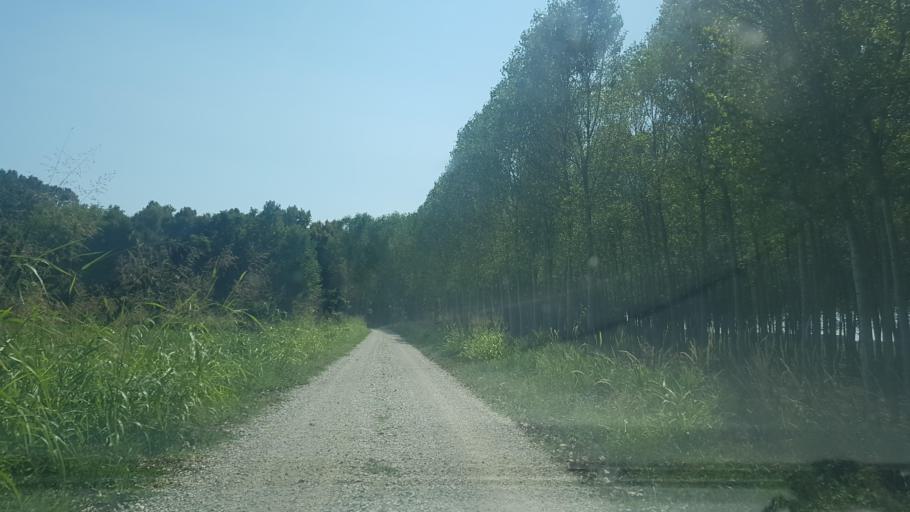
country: IT
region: Friuli Venezia Giulia
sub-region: Provincia di Udine
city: Muzzana del Turgnano
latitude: 45.8458
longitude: 13.1358
